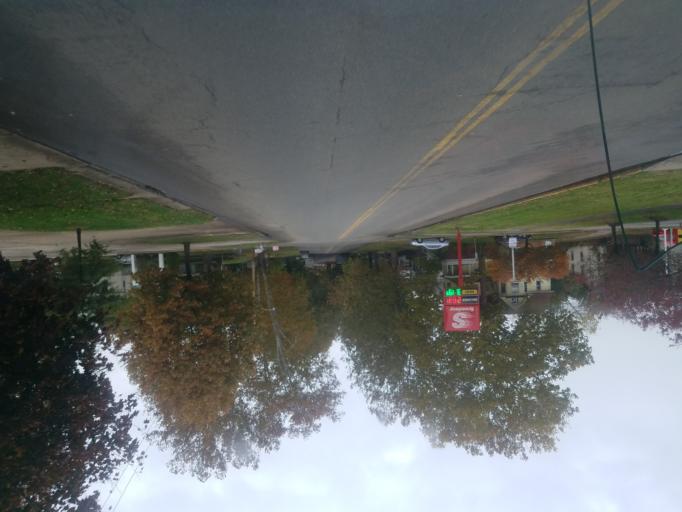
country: US
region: Ohio
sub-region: Washington County
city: Marietta
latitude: 39.4188
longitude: -81.4582
